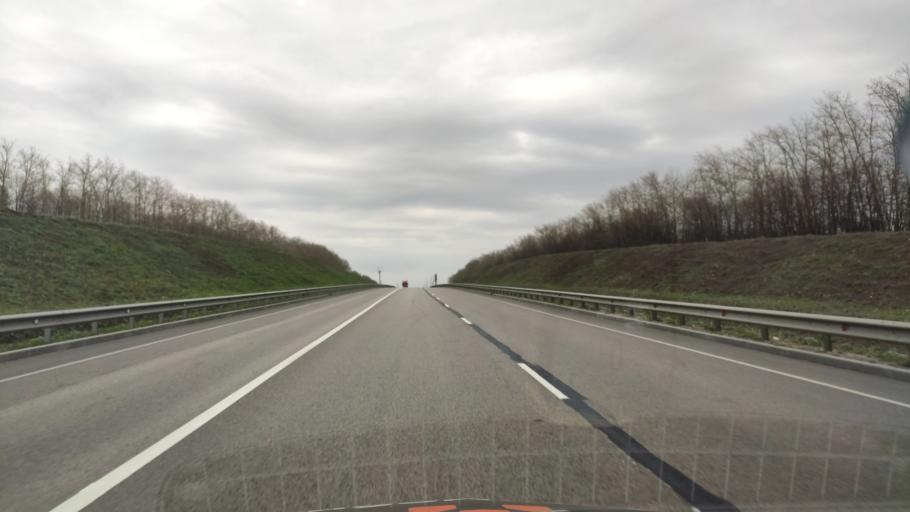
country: RU
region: Voronezj
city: Nizhnedevitsk
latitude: 51.5580
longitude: 38.2380
